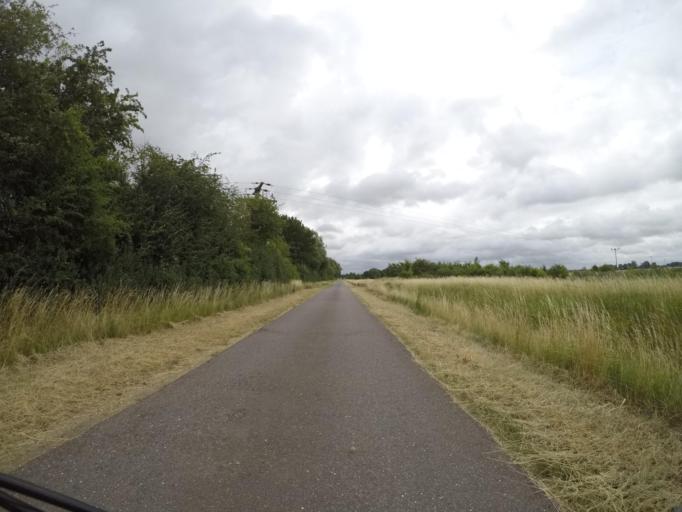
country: DE
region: Lower Saxony
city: Hitzacker
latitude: 53.1644
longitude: 11.1064
